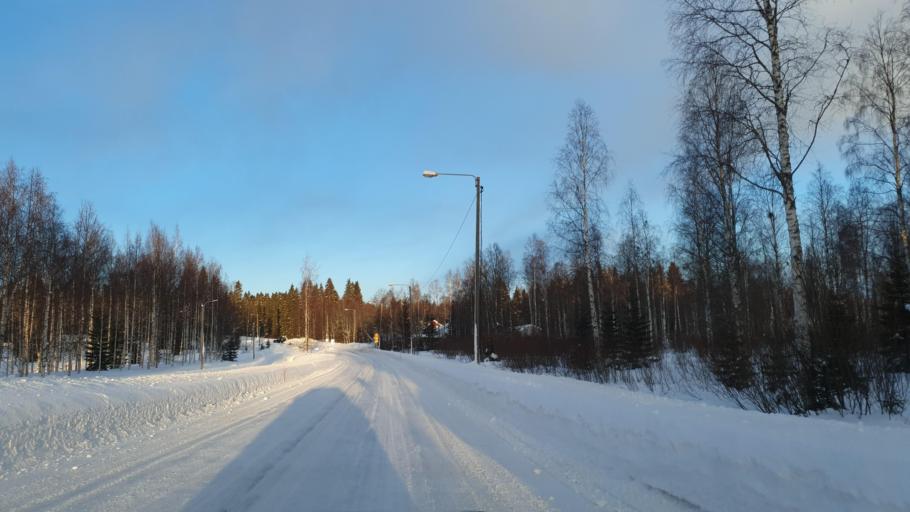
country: FI
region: Kainuu
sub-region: Kajaani
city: Ristijaervi
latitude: 64.3382
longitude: 28.1078
